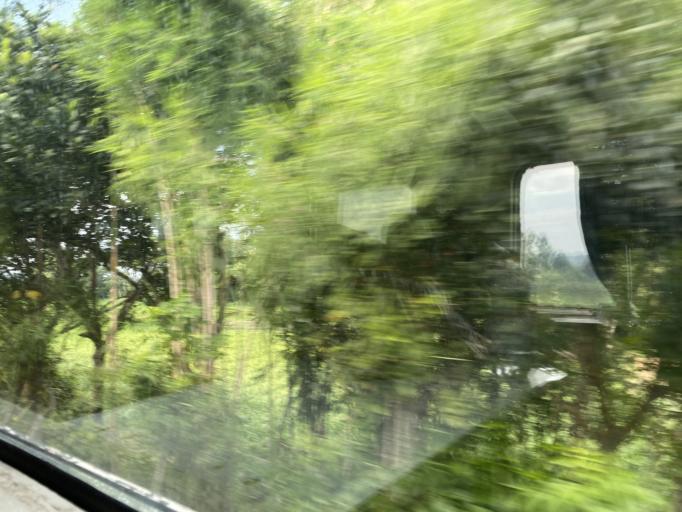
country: IN
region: Tripura
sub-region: West Tripura
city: Agartala
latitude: 23.9981
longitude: 91.2904
